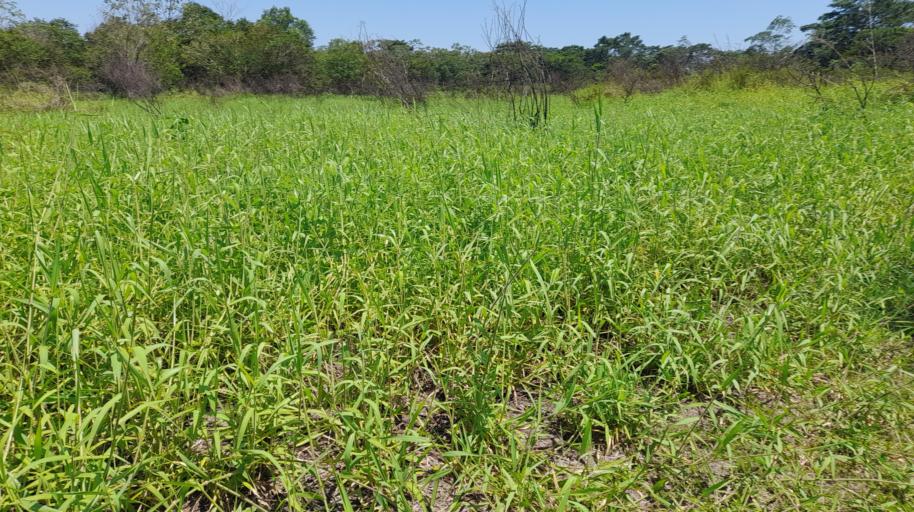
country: PE
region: Ucayali
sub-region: Provincia de Coronel Portillo
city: Puerto Callao
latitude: -8.2660
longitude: -74.6422
